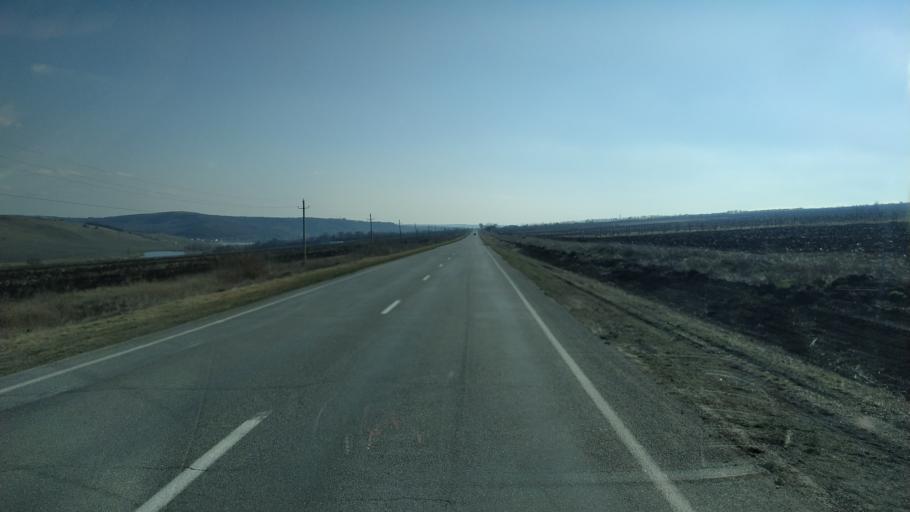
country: MD
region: Hincesti
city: Hincesti
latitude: 46.7694
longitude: 28.5235
